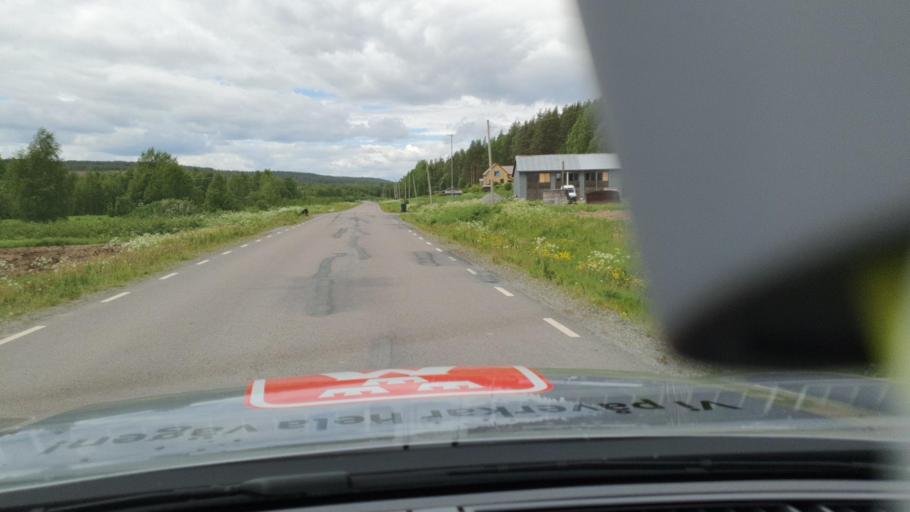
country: SE
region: Norrbotten
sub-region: Lulea Kommun
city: Sodra Sunderbyn
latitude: 65.8402
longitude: 21.9388
